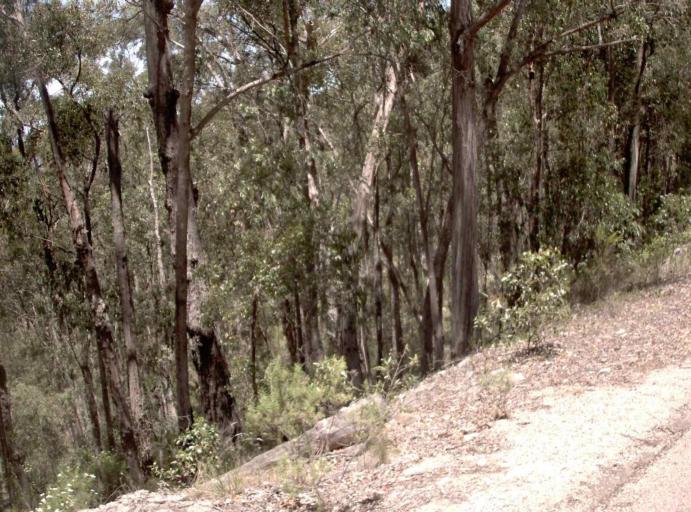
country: AU
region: Victoria
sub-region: East Gippsland
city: Lakes Entrance
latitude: -37.6076
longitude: 147.8820
